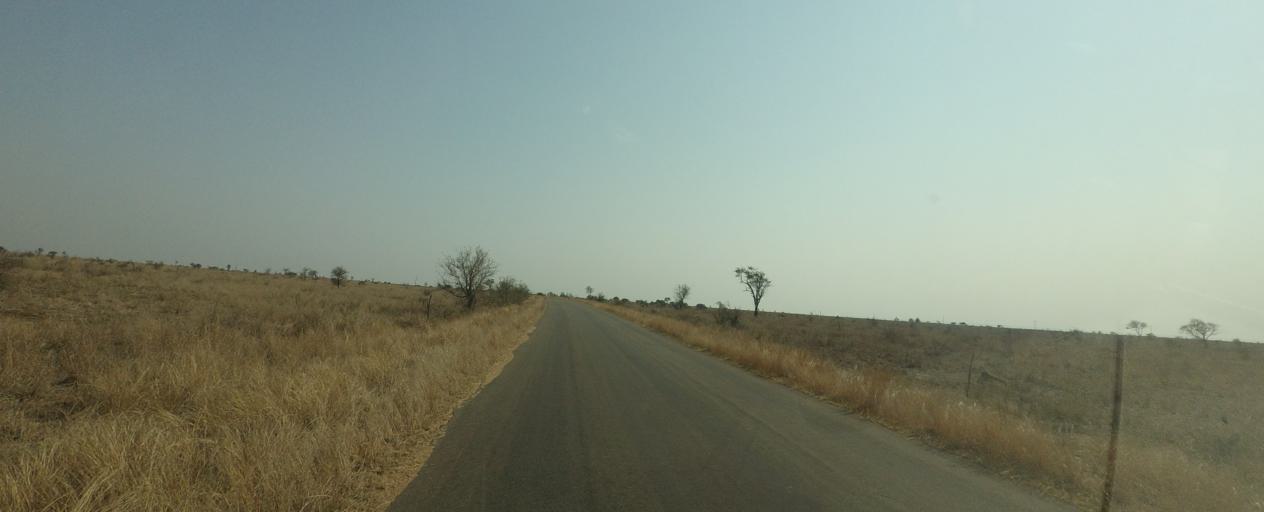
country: ZA
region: Limpopo
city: Thulamahashi
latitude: -24.3583
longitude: 31.7639
